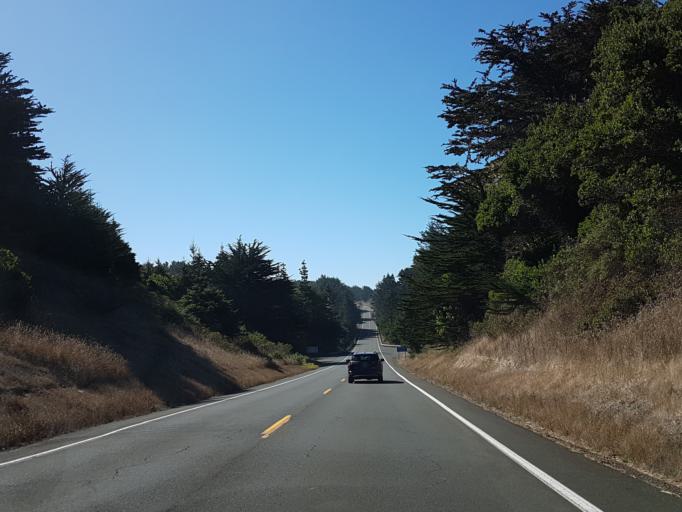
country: US
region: California
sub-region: Mendocino County
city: Boonville
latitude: 39.0369
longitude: -123.6865
